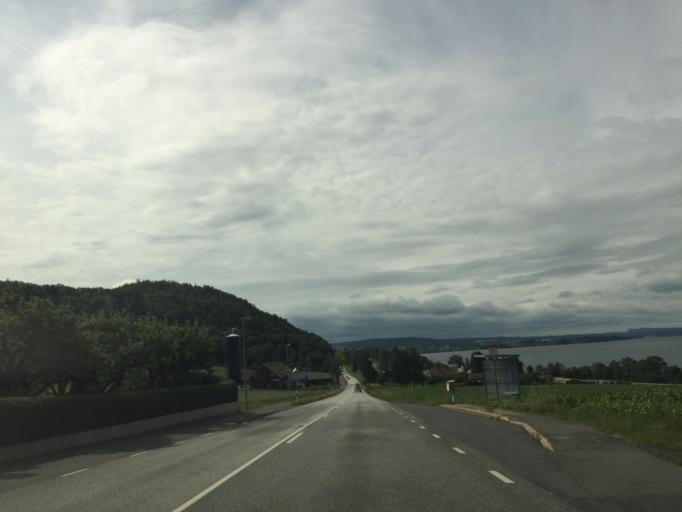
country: SE
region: Joenkoeping
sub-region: Jonkopings Kommun
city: Kaxholmen
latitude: 57.8365
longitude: 14.2726
